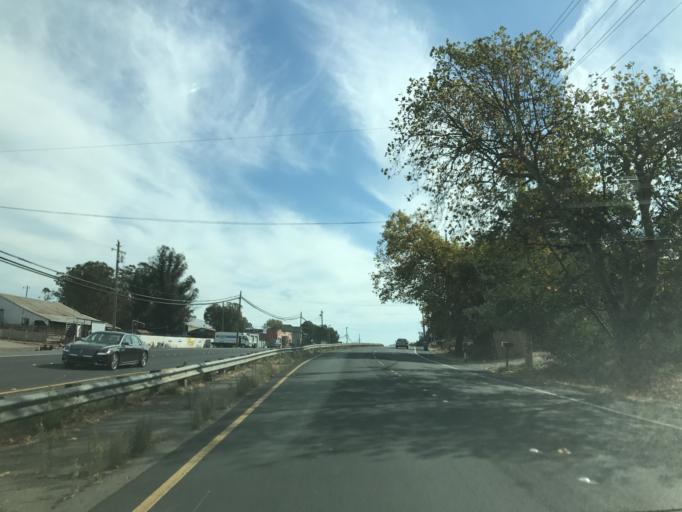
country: US
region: California
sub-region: Sonoma County
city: Petaluma
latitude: 38.2518
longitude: -122.6482
